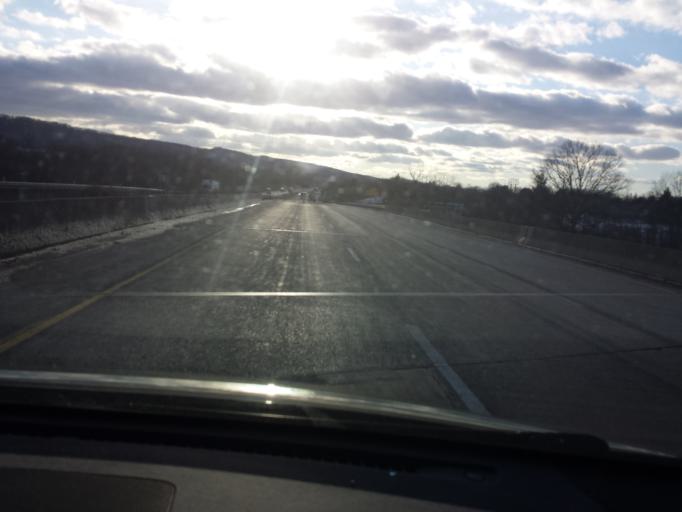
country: US
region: Pennsylvania
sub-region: Northumberland County
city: Riverside
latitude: 40.9964
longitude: -76.6447
